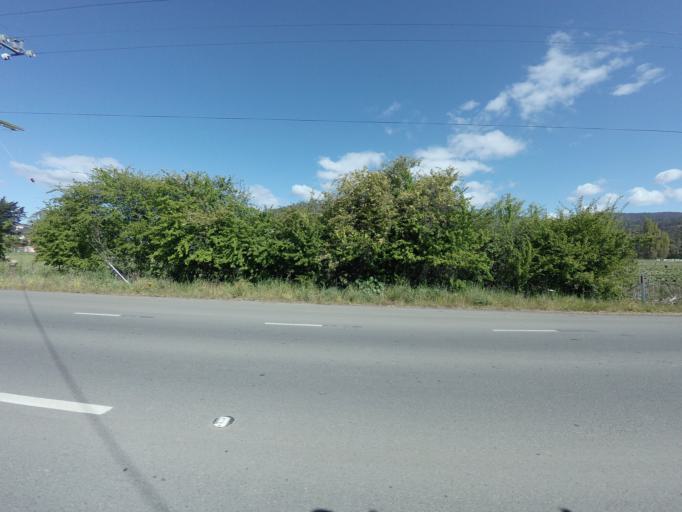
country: AU
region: Tasmania
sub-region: Derwent Valley
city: New Norfolk
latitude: -42.7778
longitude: 147.0505
